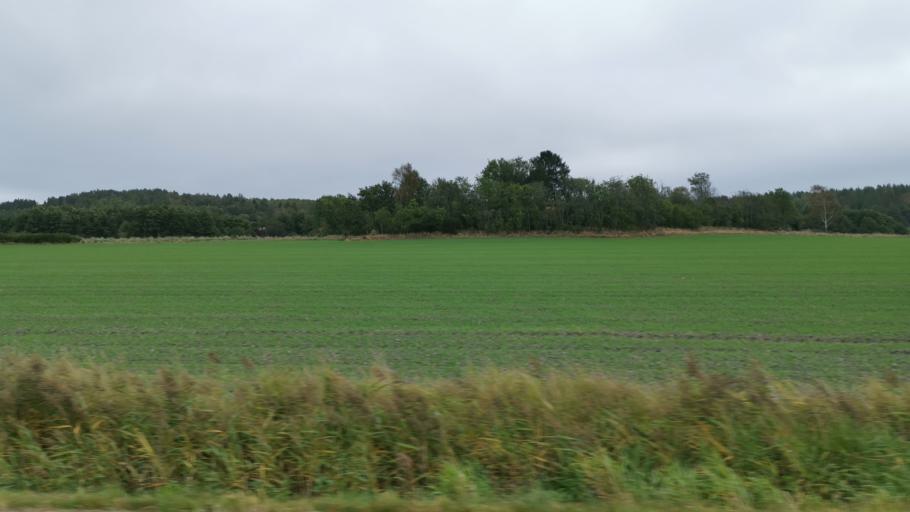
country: SE
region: Vaestra Goetaland
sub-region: Tanums Kommun
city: Tanumshede
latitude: 58.6225
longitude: 11.3551
